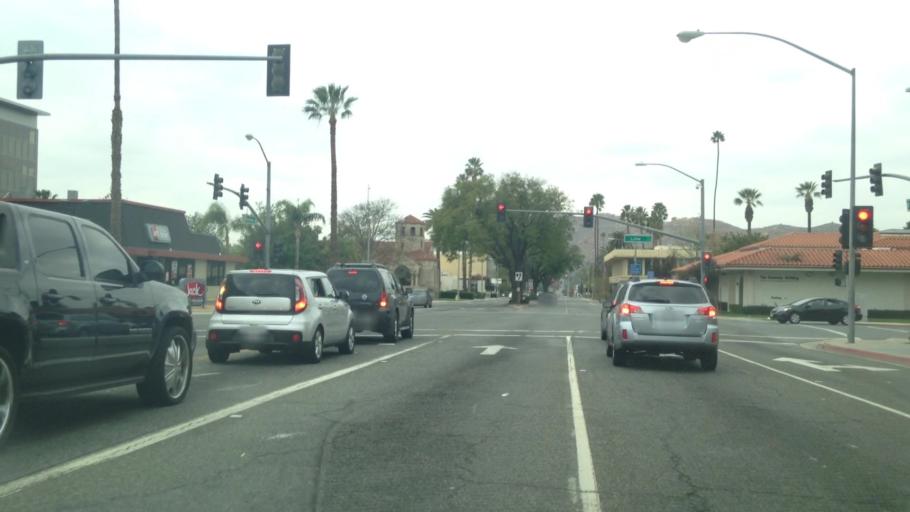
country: US
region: California
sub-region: Riverside County
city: Riverside
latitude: 33.9744
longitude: -117.3743
